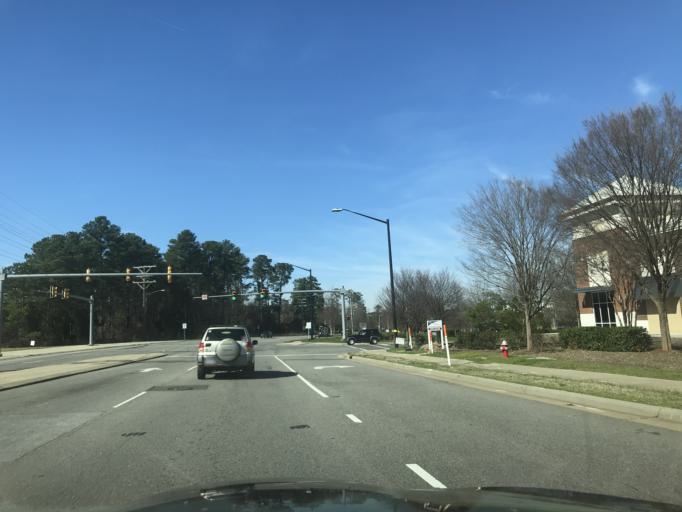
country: US
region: North Carolina
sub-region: Wake County
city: Morrisville
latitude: 35.8678
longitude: -78.8498
